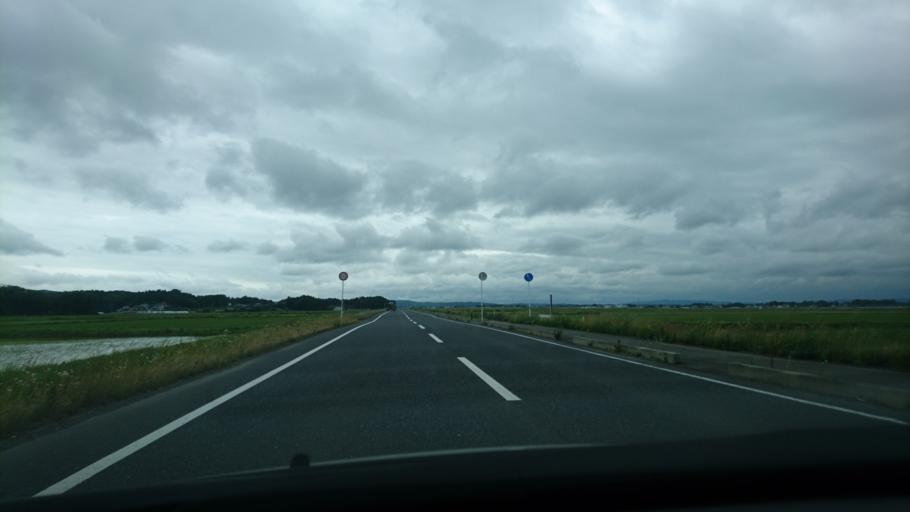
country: JP
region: Miyagi
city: Wakuya
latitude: 38.7057
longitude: 141.2601
